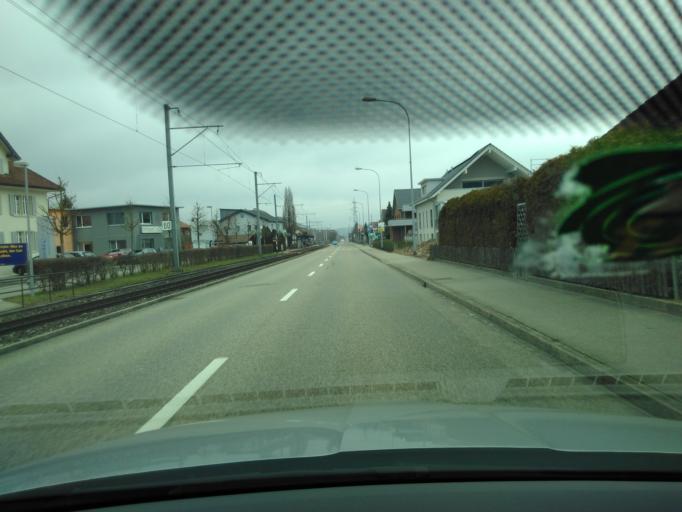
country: CH
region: Aargau
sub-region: Bezirk Aarau
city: Muhen
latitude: 47.3423
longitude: 8.0535
